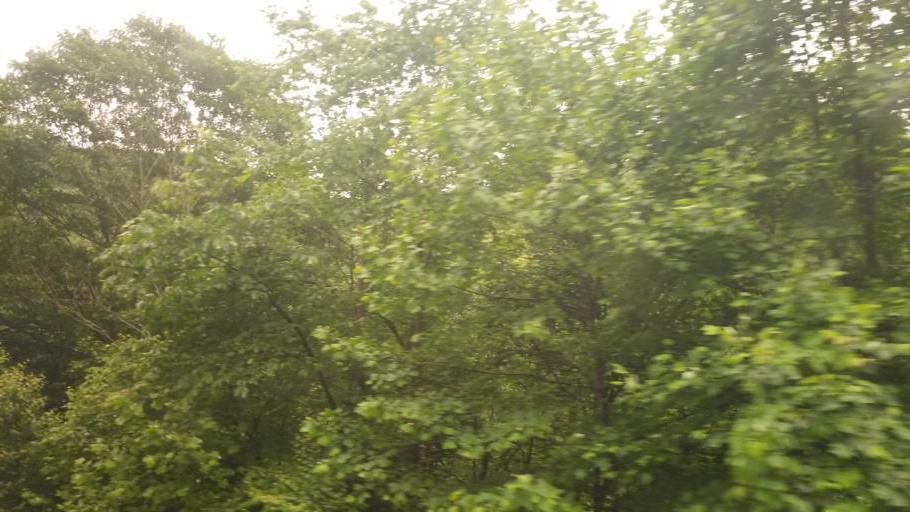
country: US
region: Pennsylvania
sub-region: Fayette County
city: South Connellsville
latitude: 39.9052
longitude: -79.4863
